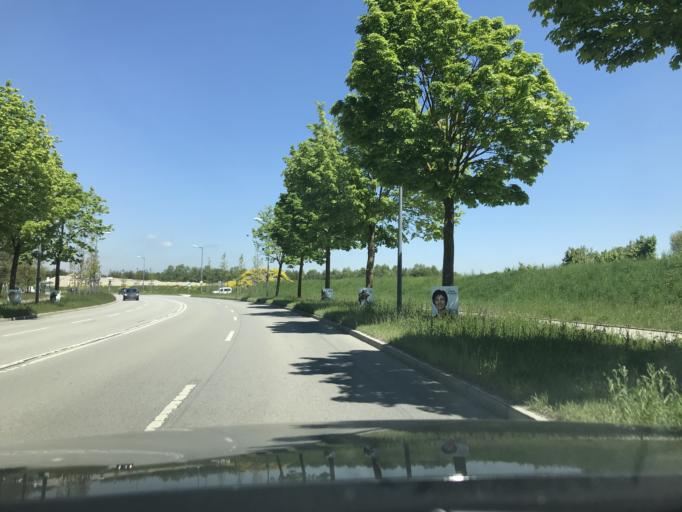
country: DE
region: Bavaria
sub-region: Upper Bavaria
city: Feldkirchen
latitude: 48.1352
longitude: 11.7150
